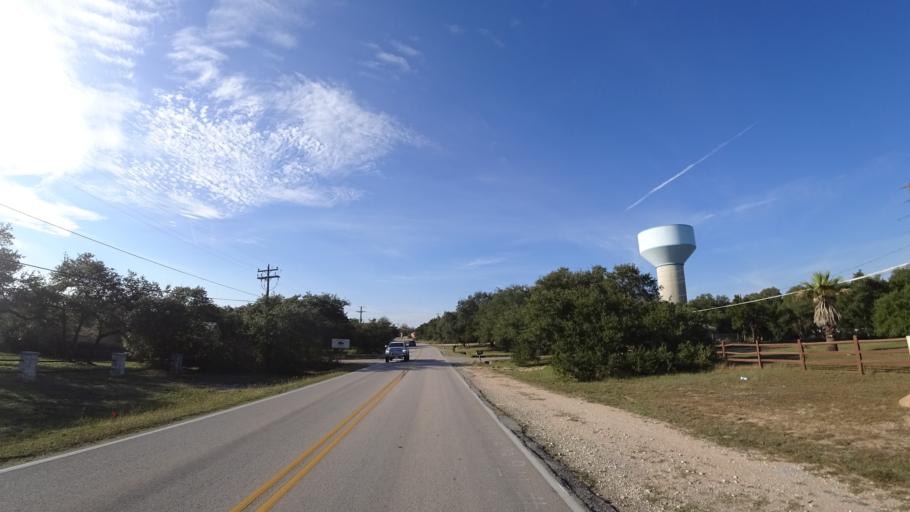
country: US
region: Texas
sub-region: Travis County
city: Bee Cave
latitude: 30.2448
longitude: -97.9251
